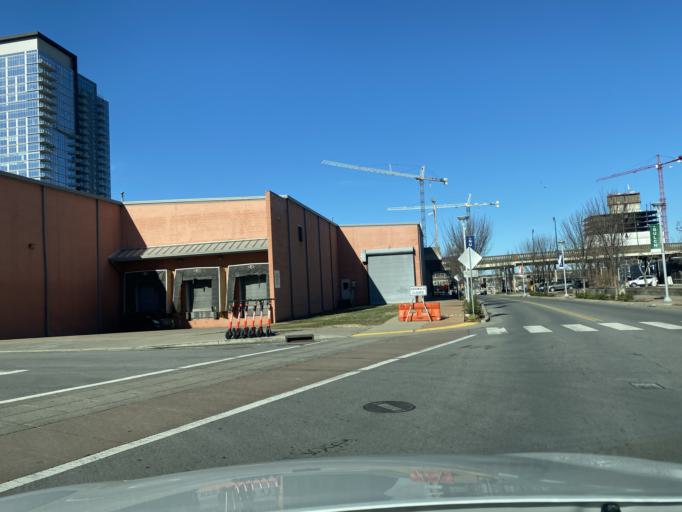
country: US
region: Tennessee
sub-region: Davidson County
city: Nashville
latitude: 36.1560
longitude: -86.7855
